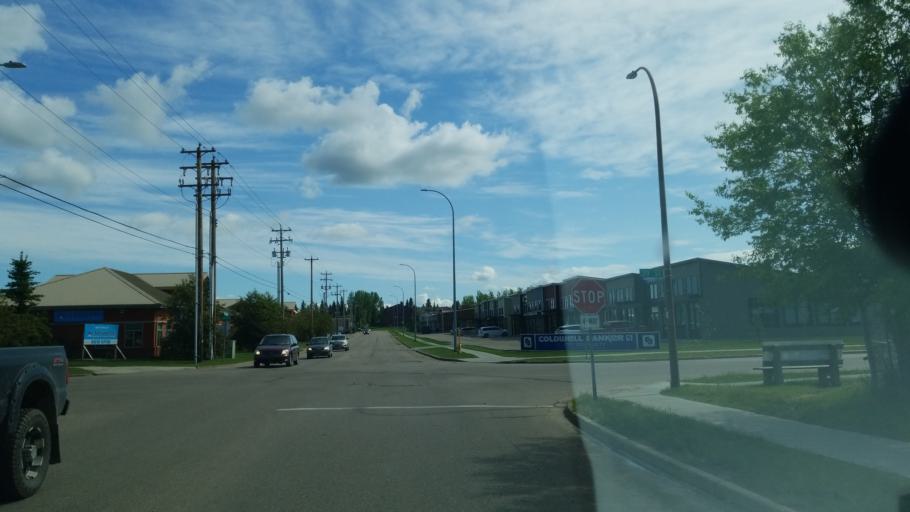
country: CA
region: Saskatchewan
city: Lloydminster
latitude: 53.2737
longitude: -110.0086
